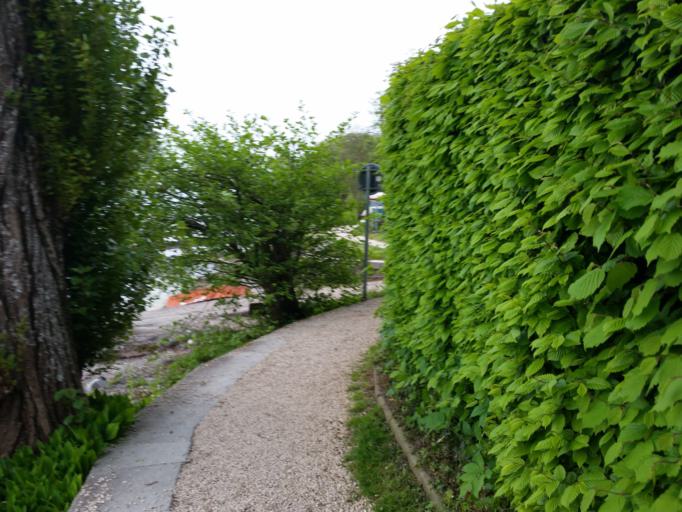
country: CH
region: Thurgau
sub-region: Arbon District
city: Uttwil
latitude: 47.5891
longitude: 9.3362
